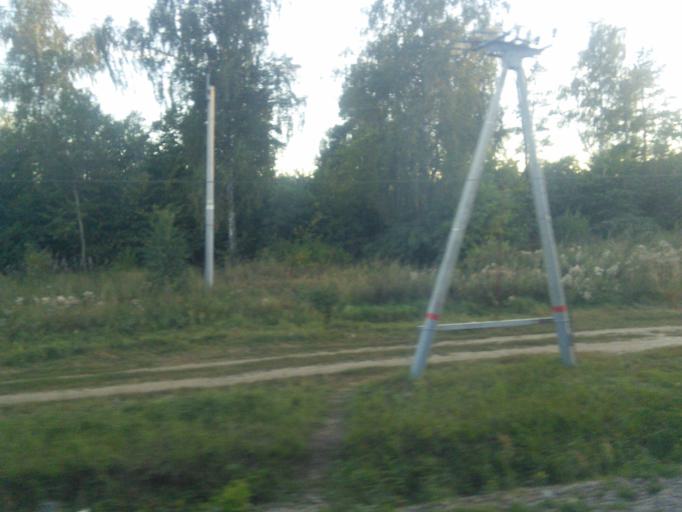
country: RU
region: Moskovskaya
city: Elektrougli
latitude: 55.7386
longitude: 38.1723
